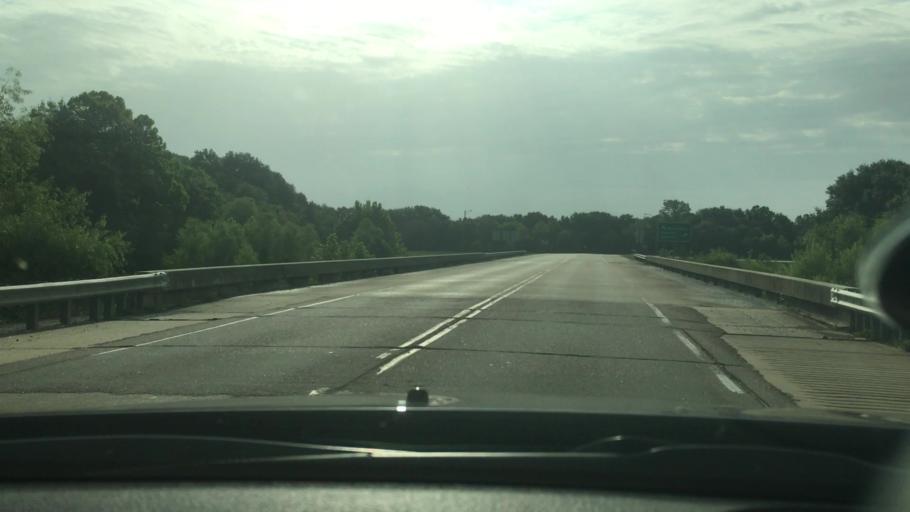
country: US
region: Oklahoma
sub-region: Atoka County
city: Atoka
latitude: 34.3935
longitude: -96.1283
